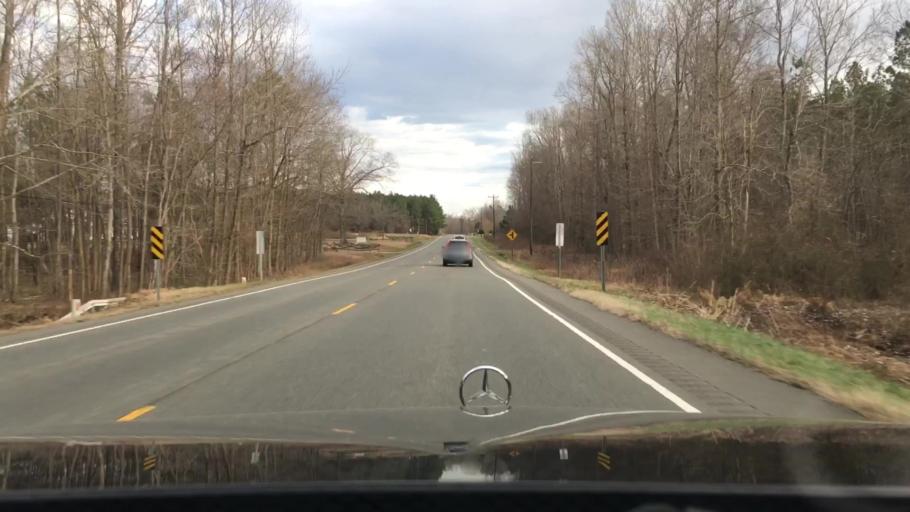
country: US
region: North Carolina
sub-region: Orange County
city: Hillsborough
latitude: 36.2057
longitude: -79.1537
